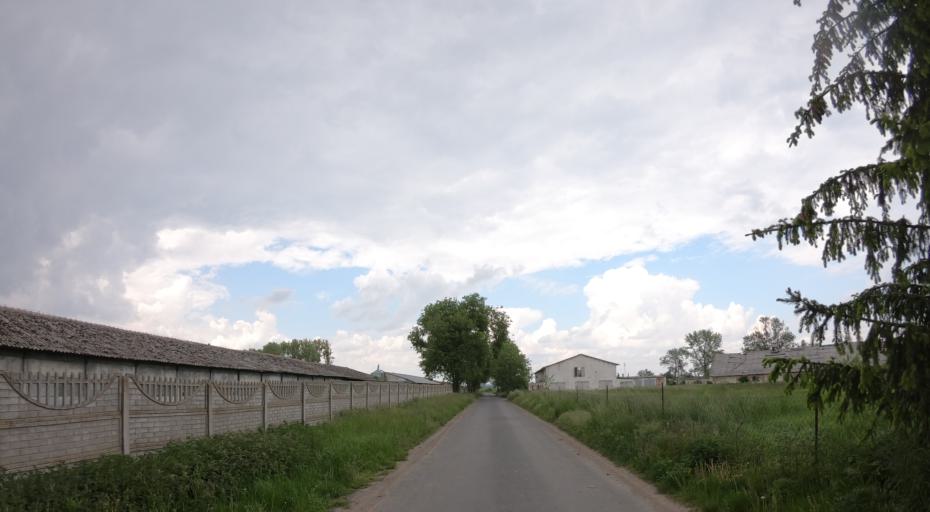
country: PL
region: West Pomeranian Voivodeship
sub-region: Powiat pyrzycki
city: Bielice
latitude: 53.2031
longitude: 14.7693
